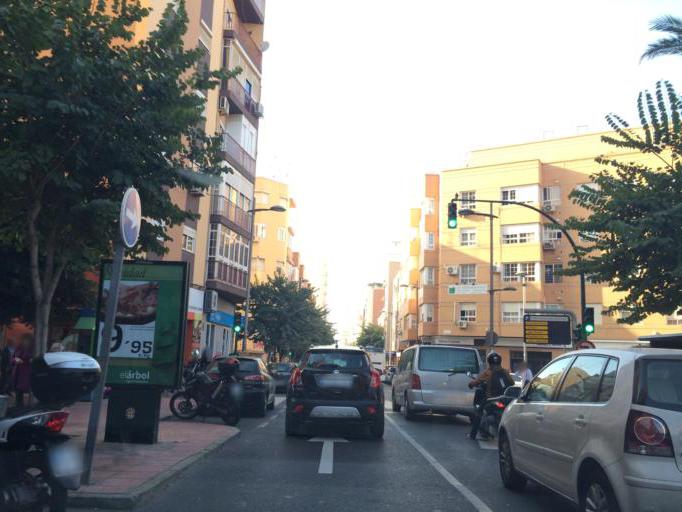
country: ES
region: Andalusia
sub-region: Provincia de Almeria
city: Almeria
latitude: 36.8482
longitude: -2.4568
